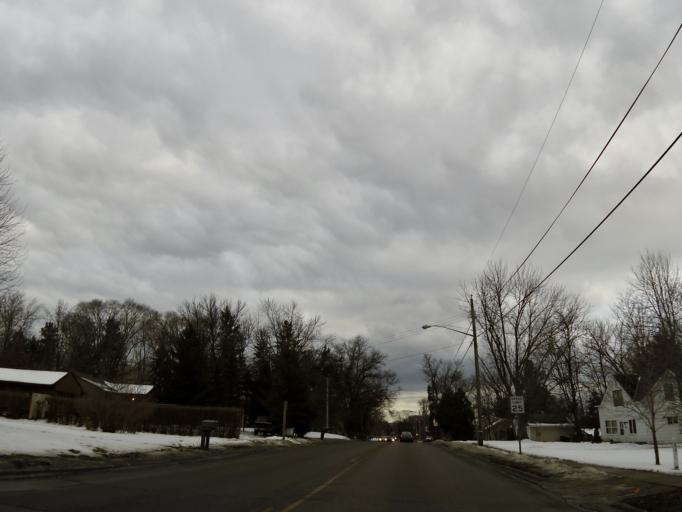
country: US
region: Wisconsin
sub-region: Saint Croix County
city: North Hudson
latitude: 44.9994
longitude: -92.7558
